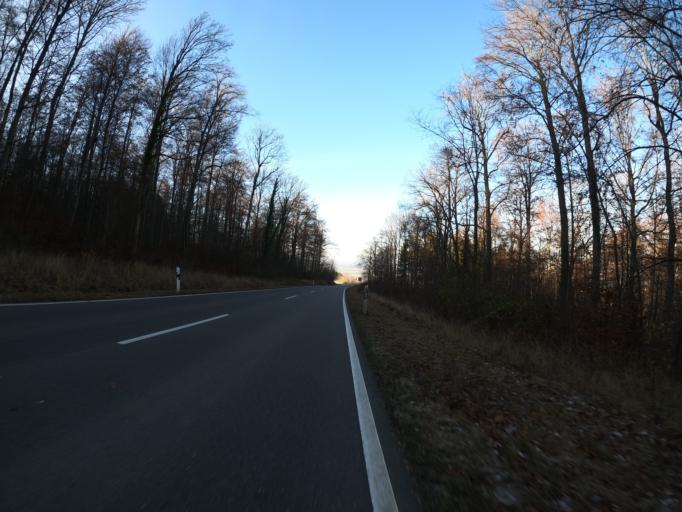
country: DE
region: Baden-Wuerttemberg
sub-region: Regierungsbezirk Stuttgart
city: Gammelshausen
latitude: 48.6323
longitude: 9.6613
